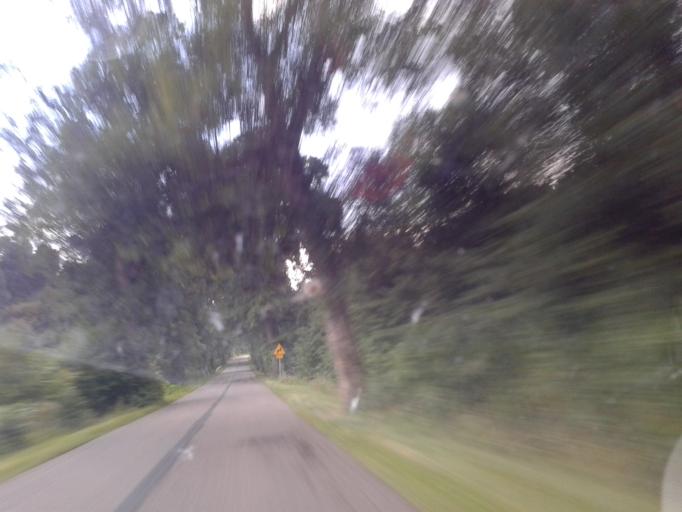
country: PL
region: West Pomeranian Voivodeship
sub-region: Powiat koszalinski
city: Bobolice
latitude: 53.9083
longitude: 16.5447
